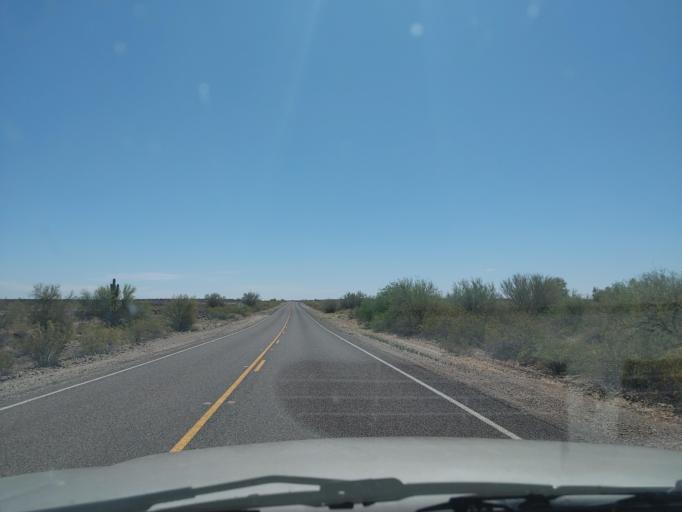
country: US
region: Arizona
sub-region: Maricopa County
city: Gila Bend
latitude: 32.9318
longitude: -113.2994
